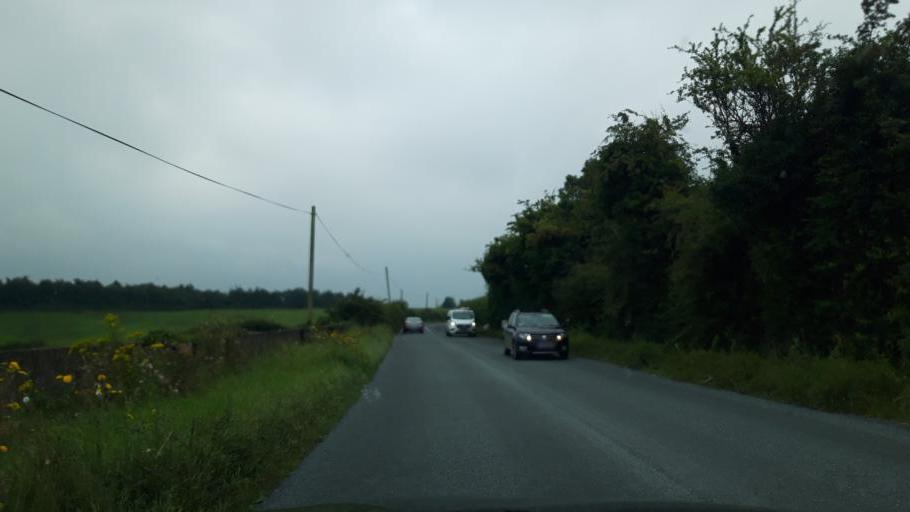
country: IE
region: Munster
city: Fethard
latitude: 52.4555
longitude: -7.7062
